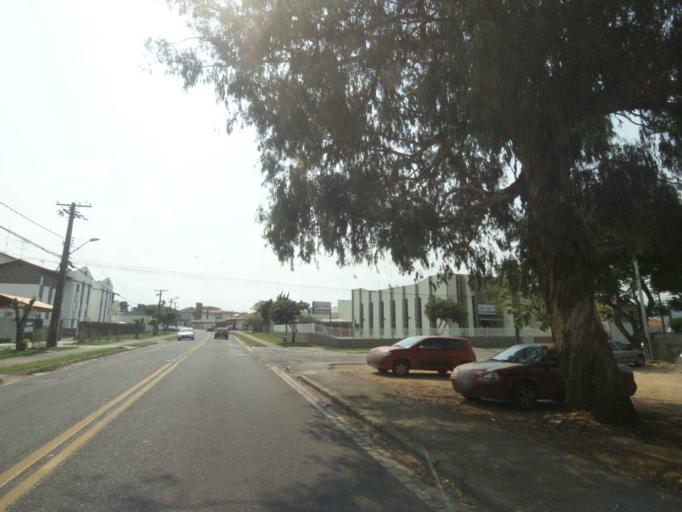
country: BR
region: Parana
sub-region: Sao Jose Dos Pinhais
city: Sao Jose dos Pinhais
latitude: -25.5329
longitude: -49.2394
